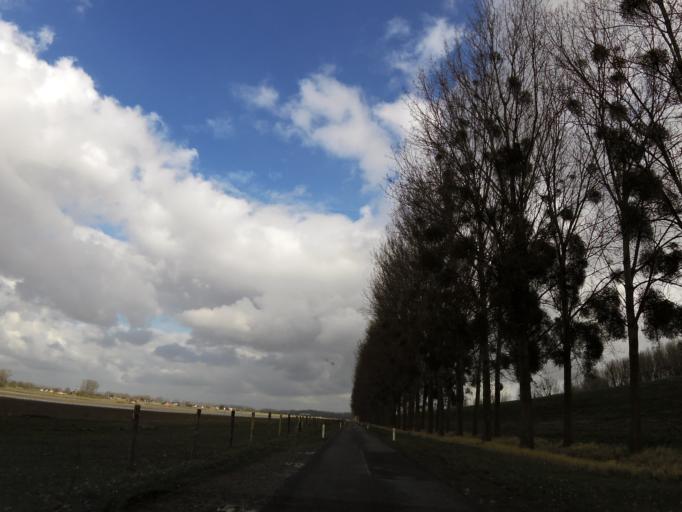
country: NL
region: Limburg
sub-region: Gemeente Stein
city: Elsloo
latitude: 50.9346
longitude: 5.7471
